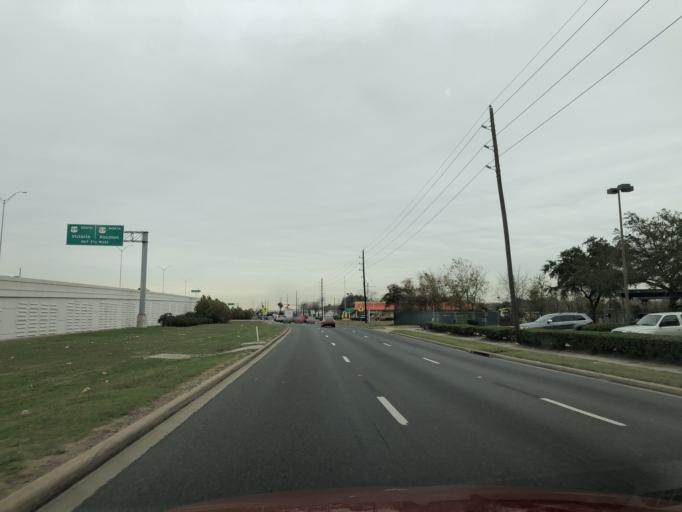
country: US
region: Texas
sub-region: Fort Bend County
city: Missouri City
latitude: 29.6429
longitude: -95.5370
